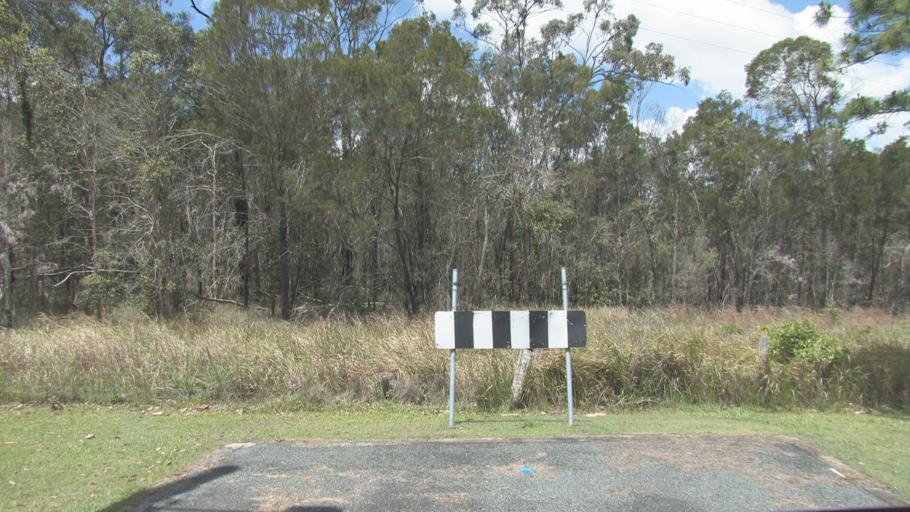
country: AU
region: Queensland
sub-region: Gold Coast
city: Yatala
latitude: -27.6602
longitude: 153.2309
